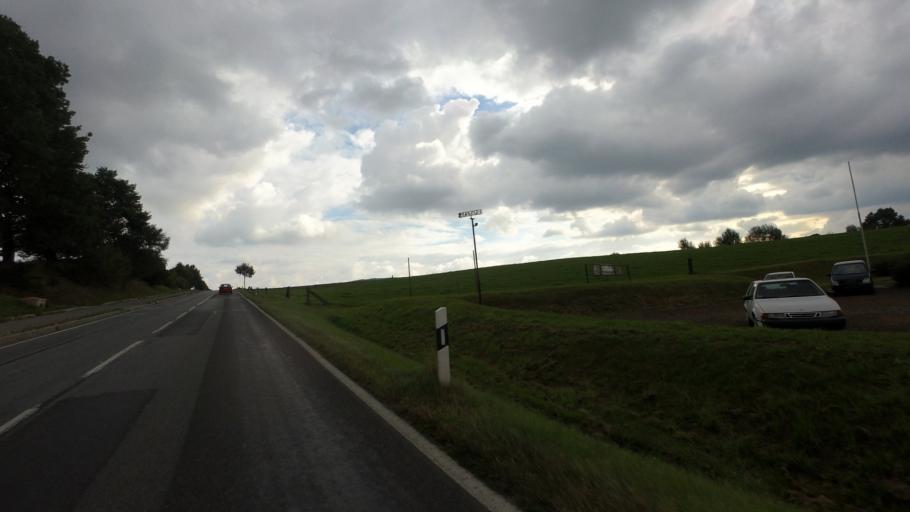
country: DE
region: Saxony
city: Crostau
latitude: 51.1058
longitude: 14.4595
